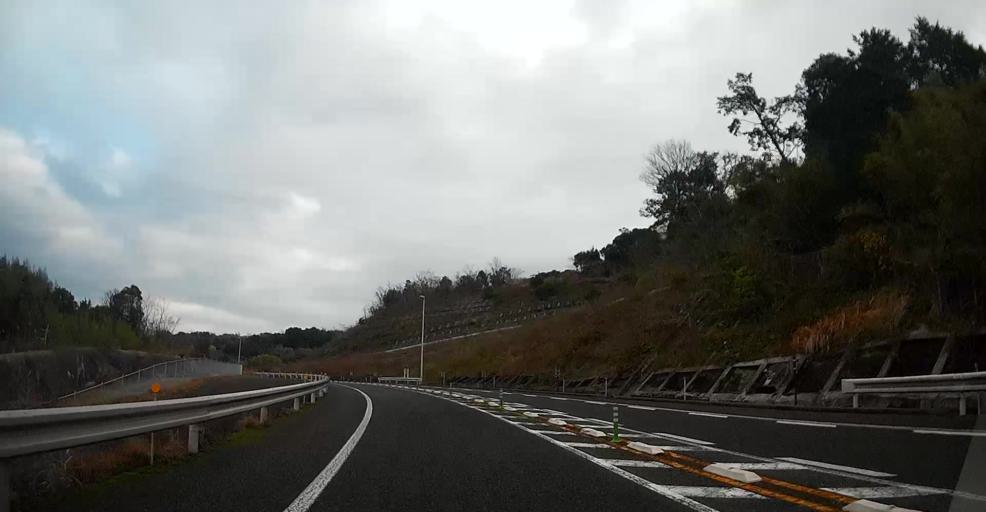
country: JP
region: Kumamoto
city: Hondo
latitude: 32.5015
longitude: 130.3065
